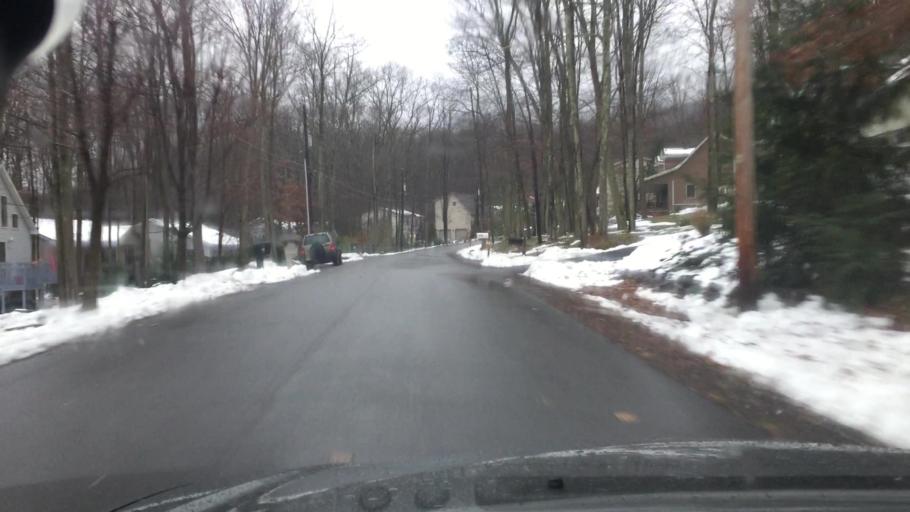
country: US
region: Pennsylvania
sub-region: Luzerne County
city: Freeland
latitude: 41.0365
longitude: -75.9386
